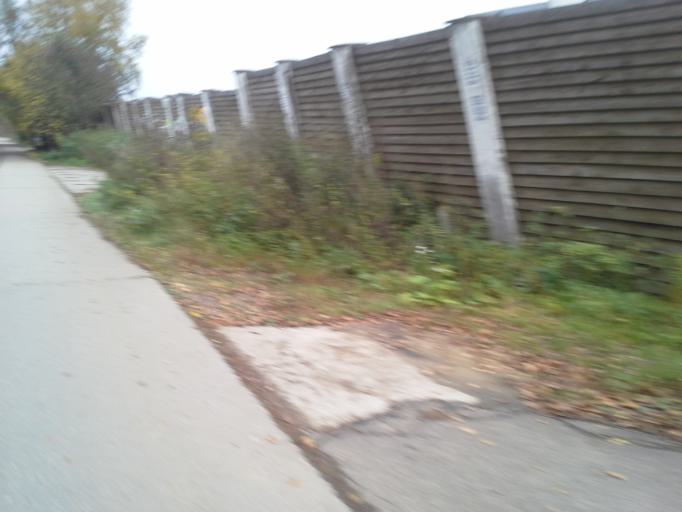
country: RU
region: Moskovskaya
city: Nazar'yevo
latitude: 55.6825
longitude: 37.0095
